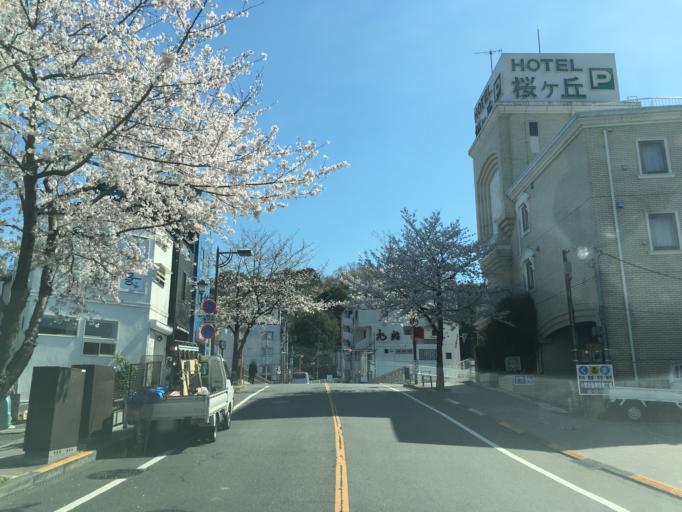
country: JP
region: Tokyo
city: Hino
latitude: 35.6480
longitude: 139.4465
